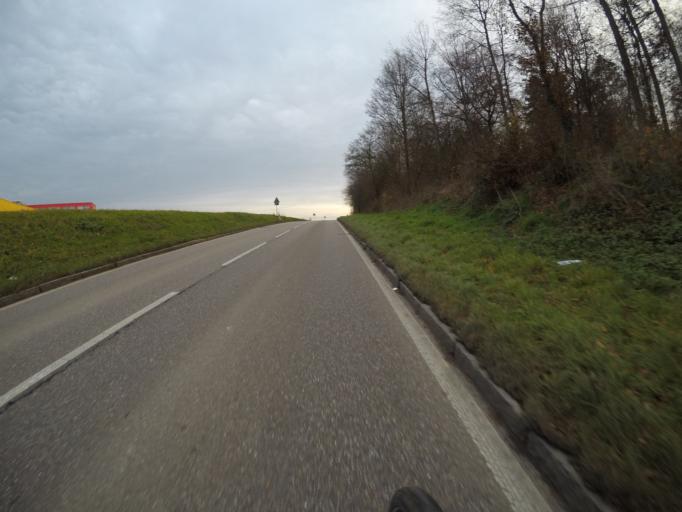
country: DE
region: Baden-Wuerttemberg
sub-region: Regierungsbezirk Stuttgart
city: Ostfildern
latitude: 48.7082
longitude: 9.2404
